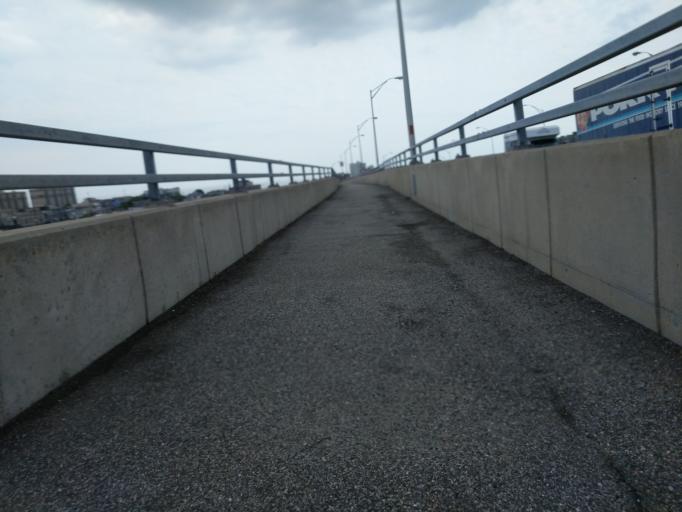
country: US
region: New York
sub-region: Nassau County
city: Inwood
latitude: 40.5916
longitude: -73.8196
